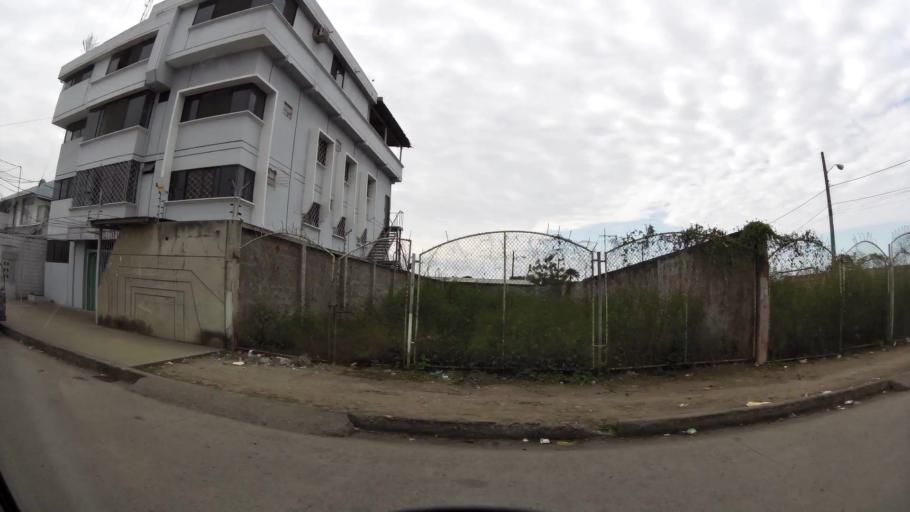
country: EC
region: El Oro
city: Machala
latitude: -3.2503
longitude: -79.9578
